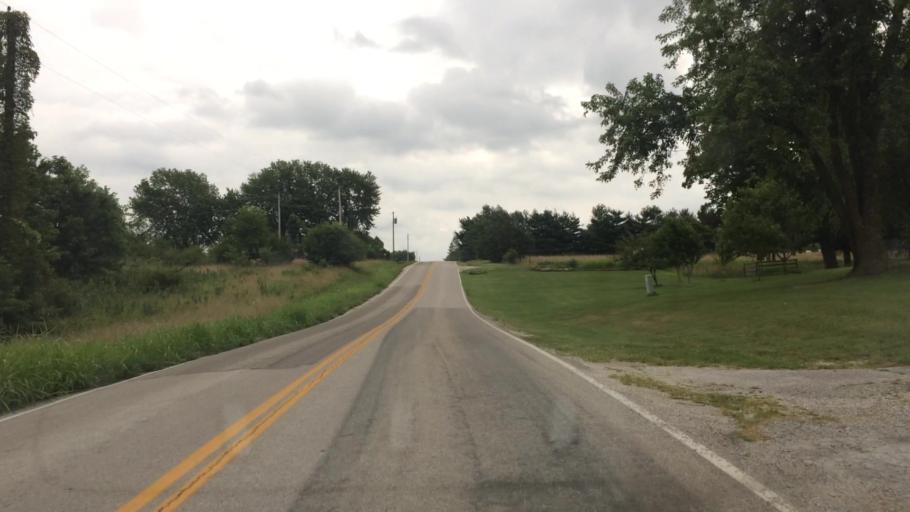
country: US
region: Missouri
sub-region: Webster County
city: Marshfield
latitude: 37.3413
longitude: -93.0036
